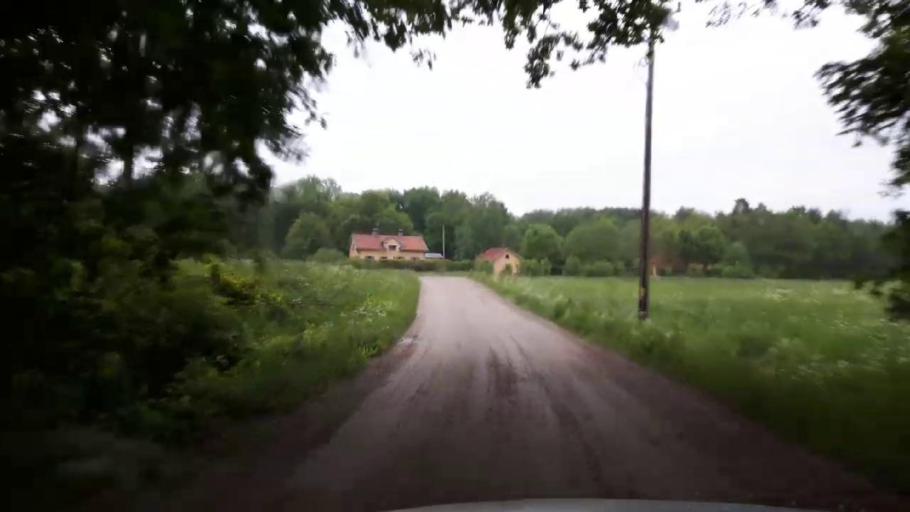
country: SE
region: Vaestmanland
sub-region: Arboga Kommun
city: Tyringe
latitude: 59.3819
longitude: 15.9345
